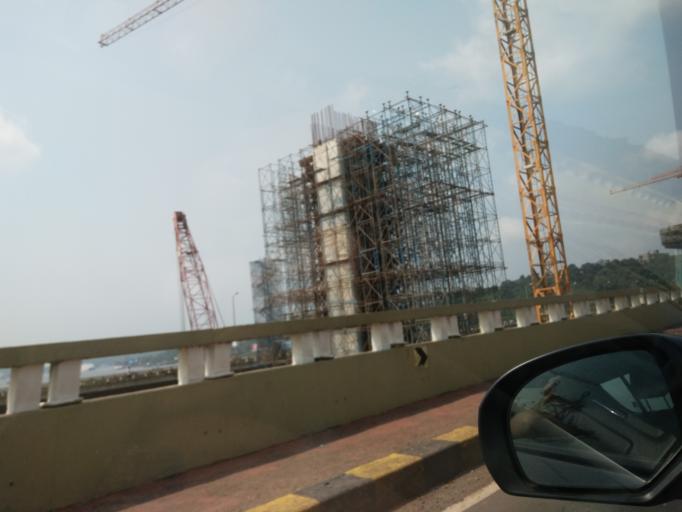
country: IN
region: Goa
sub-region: North Goa
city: Panaji
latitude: 15.5018
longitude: 73.8372
